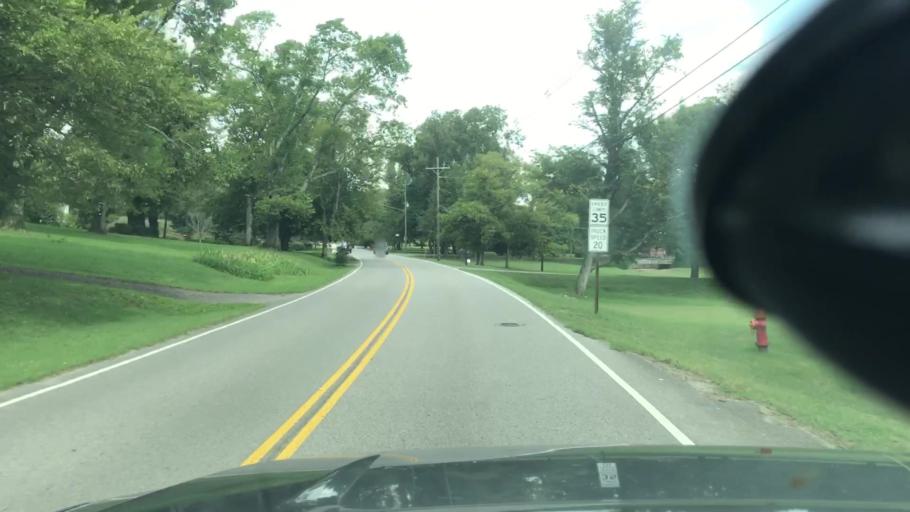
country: US
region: Tennessee
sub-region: Davidson County
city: Belle Meade
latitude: 36.0835
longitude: -86.8616
